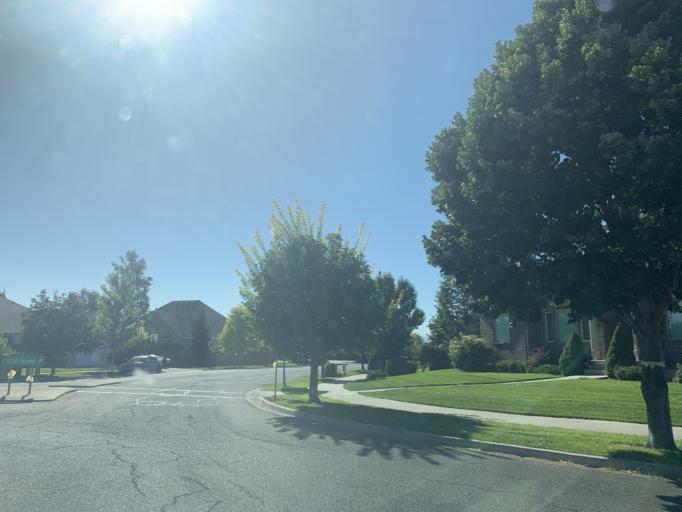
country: US
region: Utah
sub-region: Utah County
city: Provo
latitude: 40.2566
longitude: -111.6854
